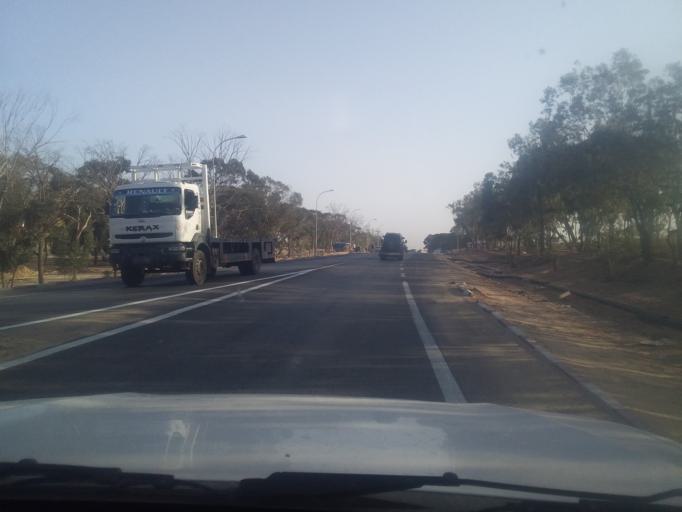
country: TN
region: Qabis
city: Gabes
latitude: 33.6348
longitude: 10.2821
